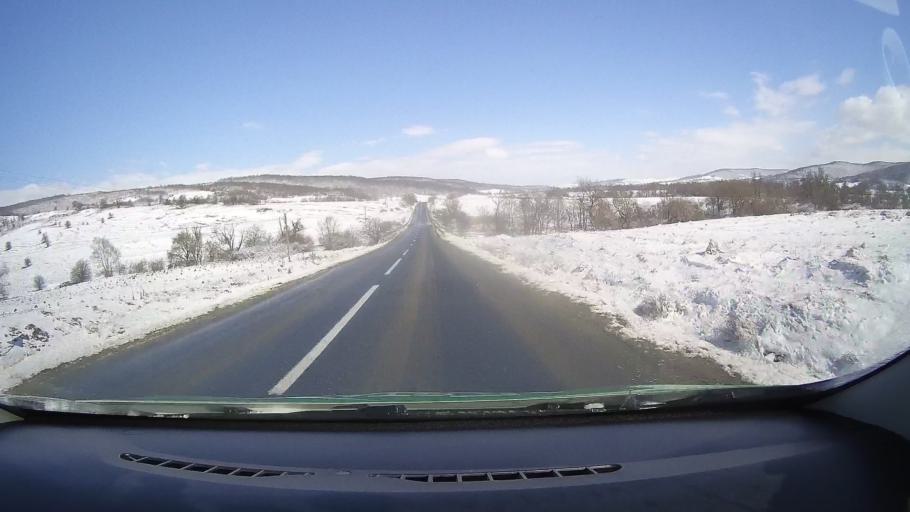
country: RO
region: Sibiu
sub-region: Comuna Rosia
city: Rosia
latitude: 45.8202
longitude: 24.3802
